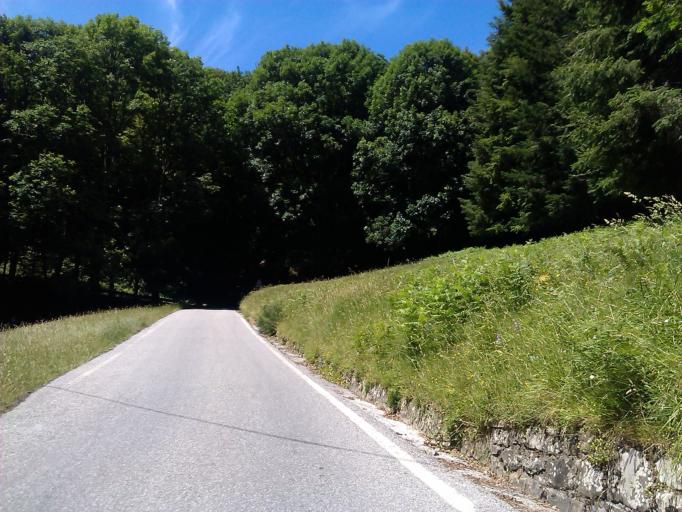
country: IT
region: Tuscany
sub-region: Provincia di Prato
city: Cantagallo
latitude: 44.0123
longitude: 11.0229
